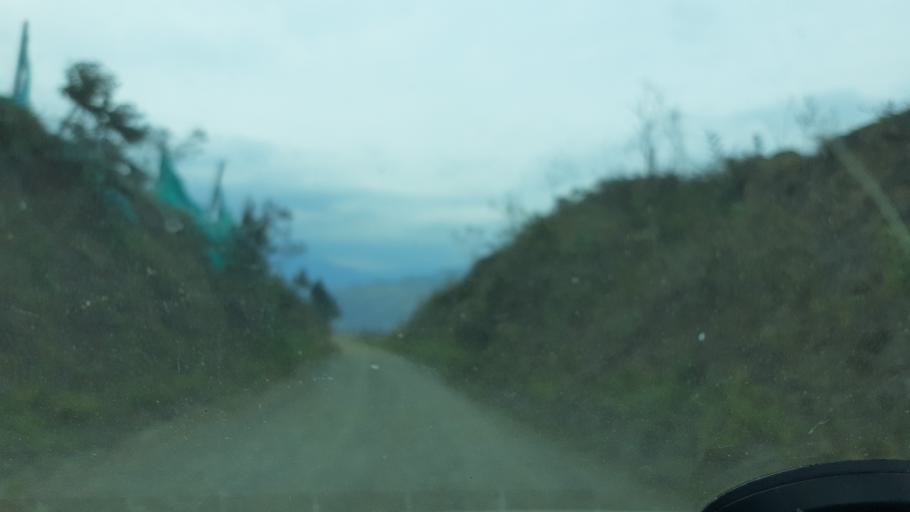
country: CO
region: Boyaca
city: Somondoco
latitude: 4.9818
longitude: -73.3753
